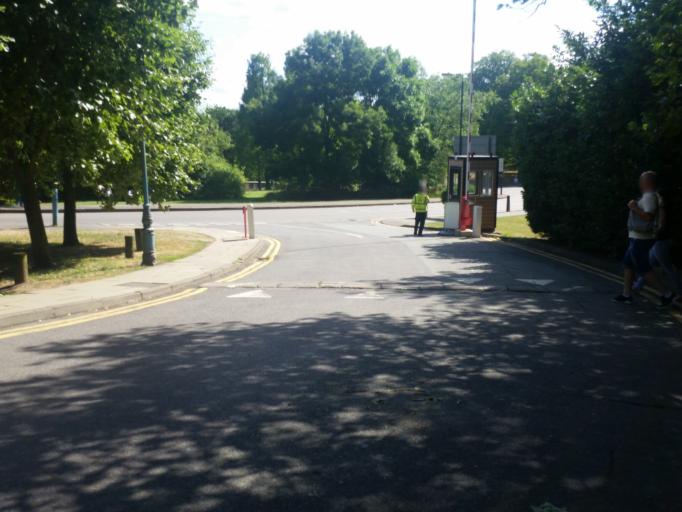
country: GB
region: England
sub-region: Greater London
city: Crouch End
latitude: 51.5934
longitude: -0.1335
